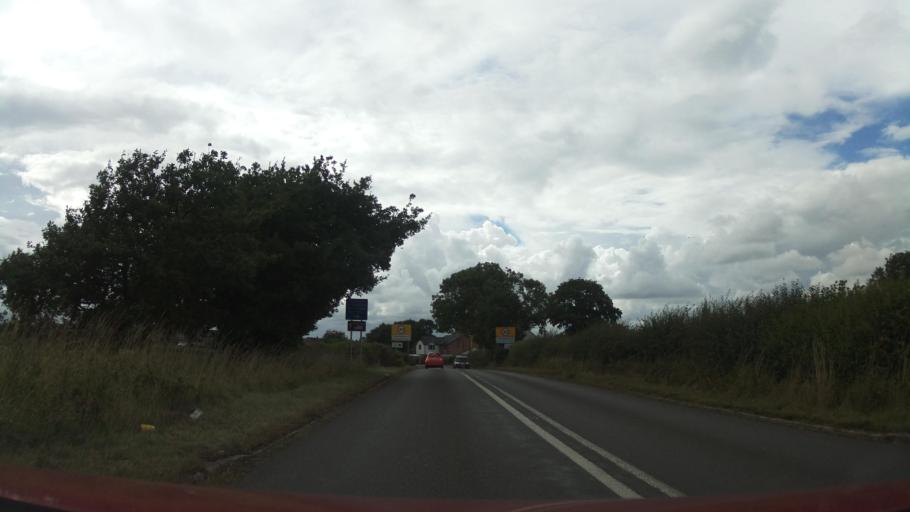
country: GB
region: England
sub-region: Staffordshire
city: Eccleshall
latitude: 52.8290
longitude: -2.2938
